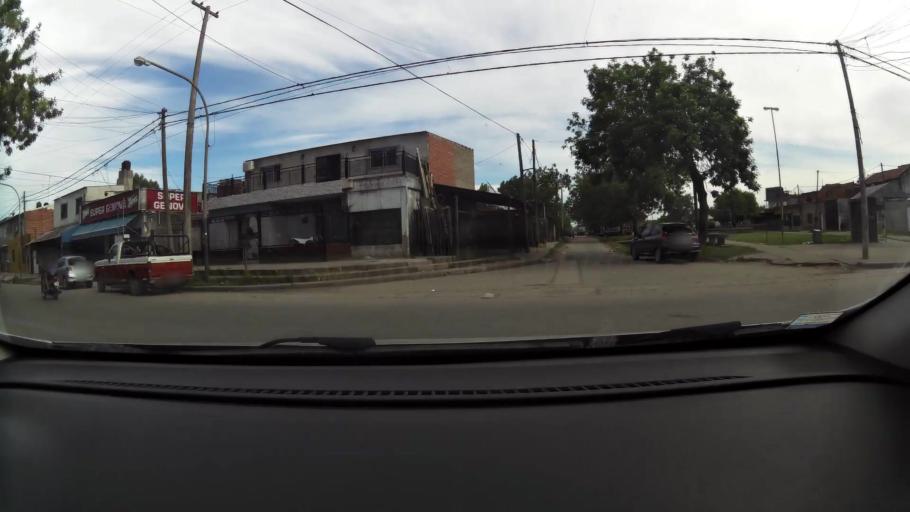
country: AR
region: Santa Fe
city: Granadero Baigorria
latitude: -32.9159
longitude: -60.7089
